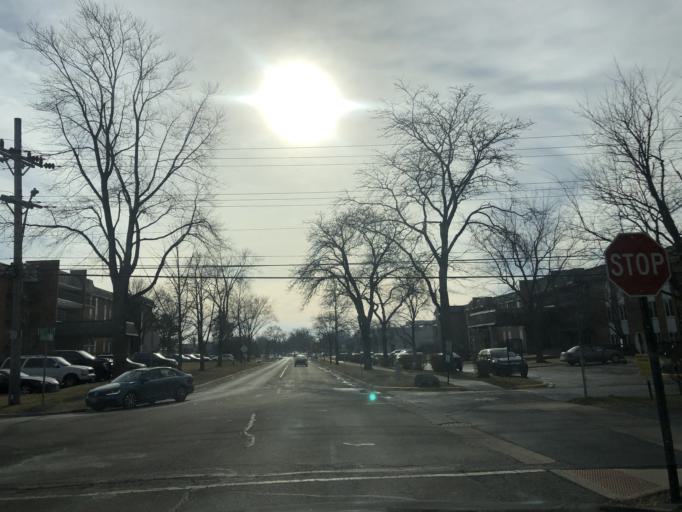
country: US
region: Illinois
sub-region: DuPage County
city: Downers Grove
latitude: 41.8113
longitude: -88.0149
